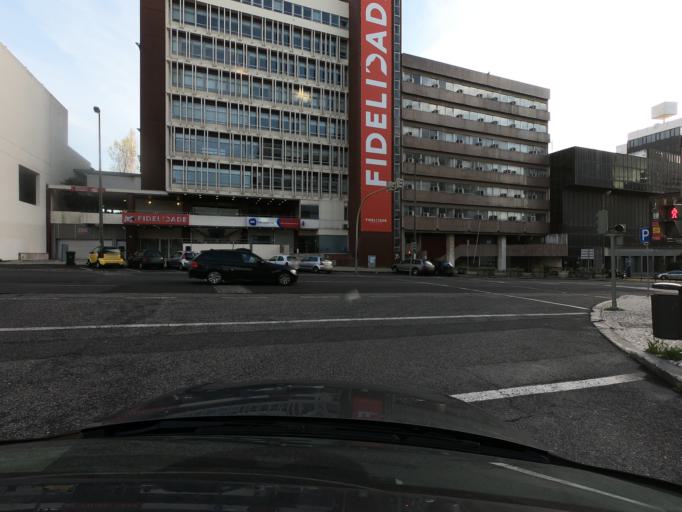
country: PT
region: Lisbon
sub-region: Lisbon
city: Lisbon
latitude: 38.7375
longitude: -9.1642
